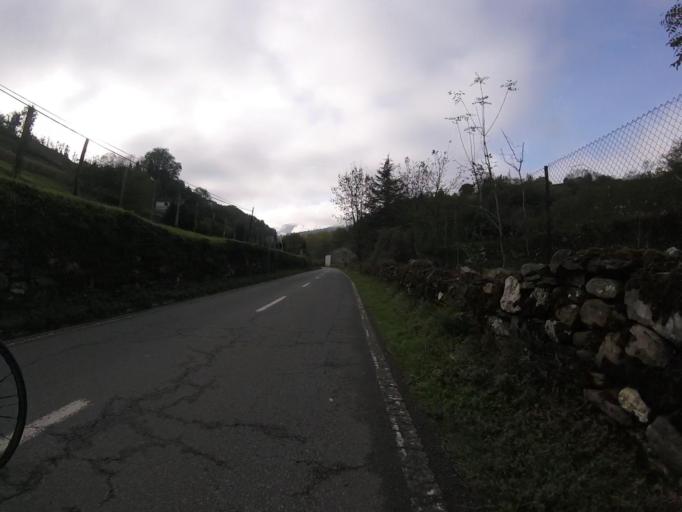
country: ES
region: Navarre
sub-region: Provincia de Navarra
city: Goizueta
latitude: 43.1802
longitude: -1.8614
